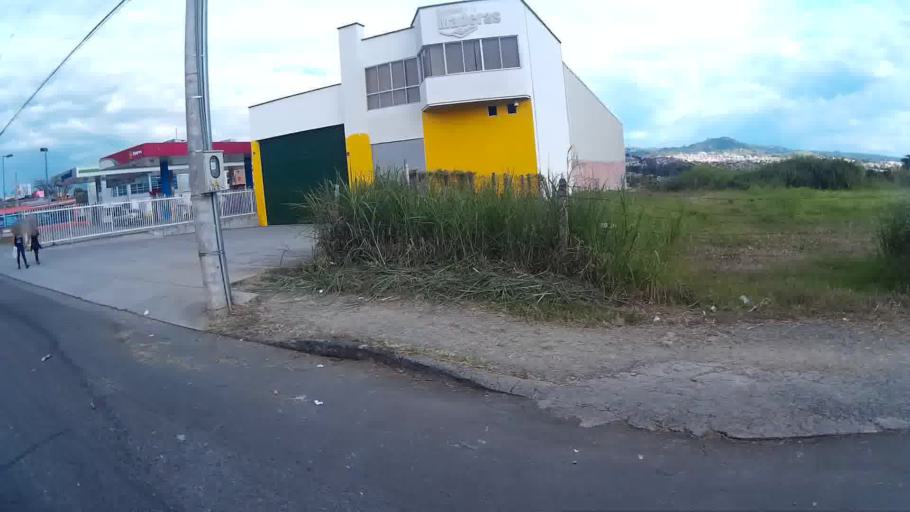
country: CO
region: Risaralda
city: Pereira
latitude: 4.8126
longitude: -75.7362
